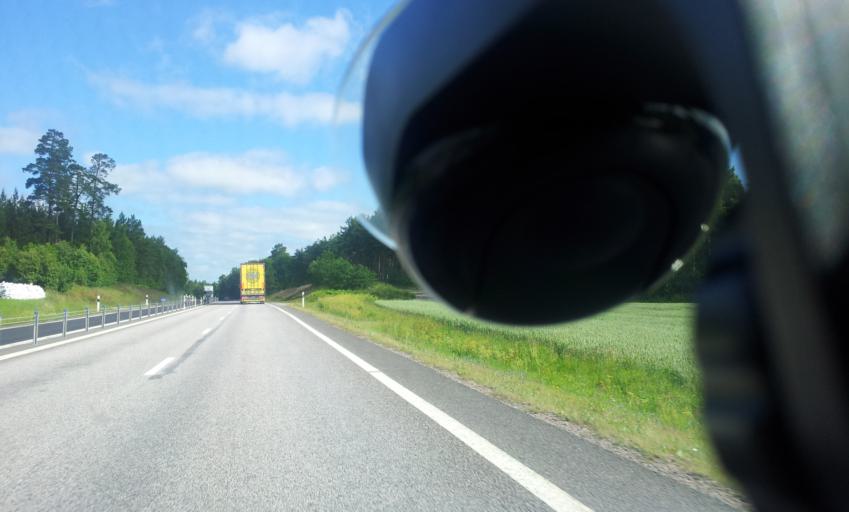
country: SE
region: Kalmar
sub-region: Kalmar Kommun
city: Lindsdal
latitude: 56.8170
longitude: 16.3696
